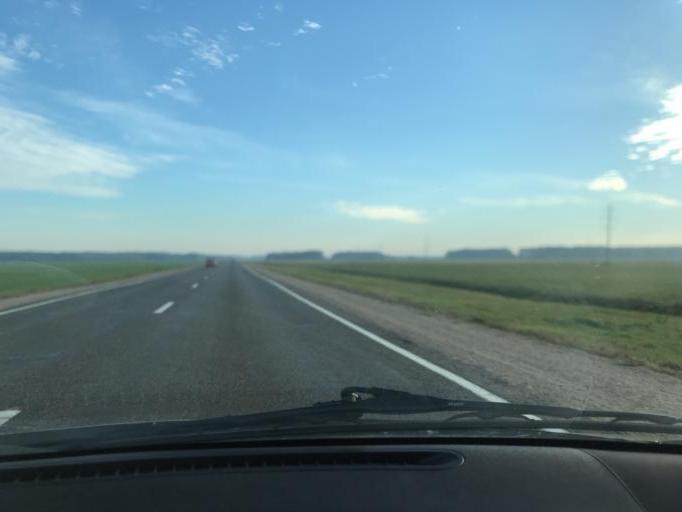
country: BY
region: Brest
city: Drahichyn
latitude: 52.2042
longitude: 25.0573
